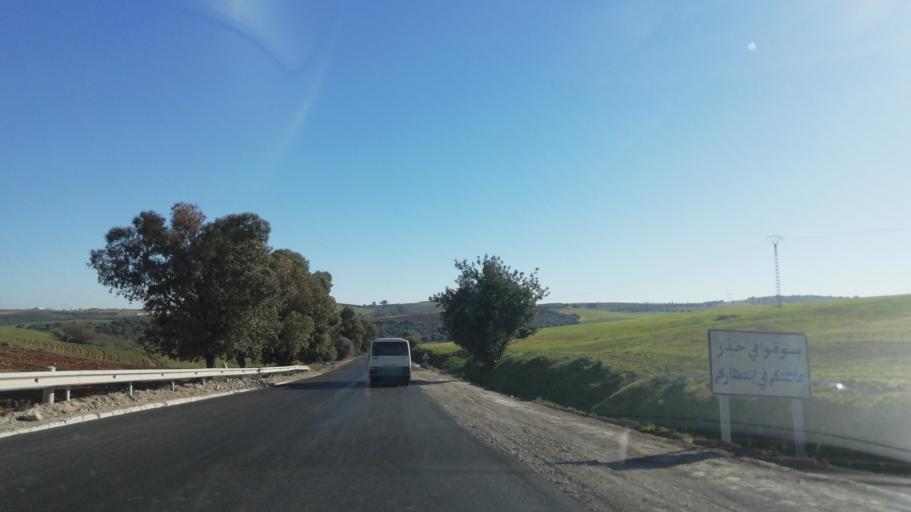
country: DZ
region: Relizane
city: Smala
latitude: 35.6721
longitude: 0.8046
